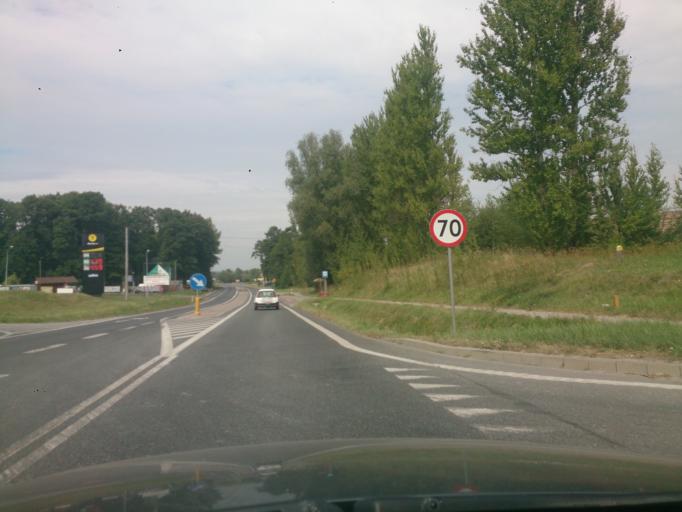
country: PL
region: Subcarpathian Voivodeship
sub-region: Powiat kolbuszowski
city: Kolbuszowa
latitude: 50.2078
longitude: 21.8279
